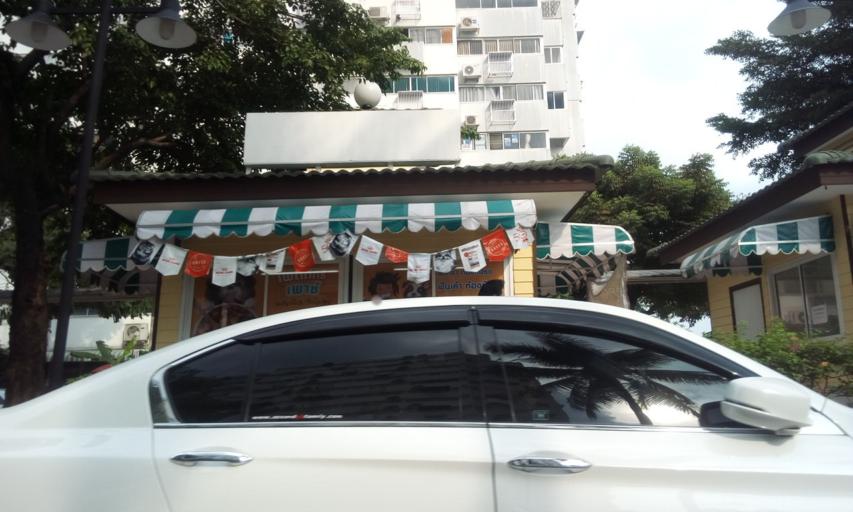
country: TH
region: Bangkok
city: Don Mueang
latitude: 13.9147
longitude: 100.5557
